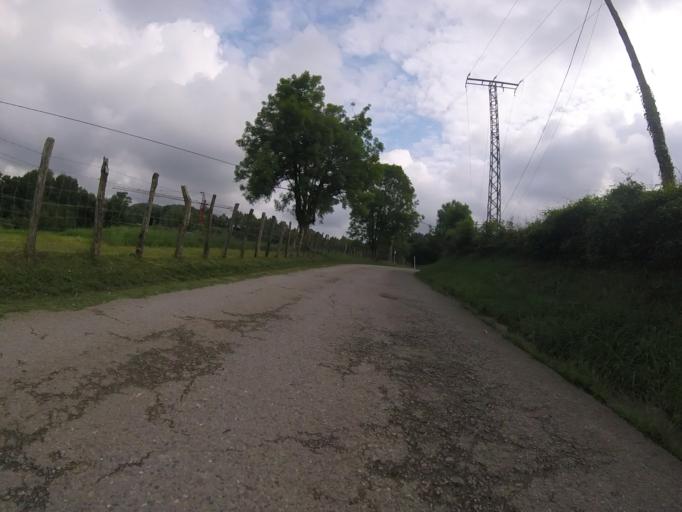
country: ES
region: Basque Country
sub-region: Provincia de Guipuzcoa
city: Astigarraga
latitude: 43.3008
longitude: -1.9329
